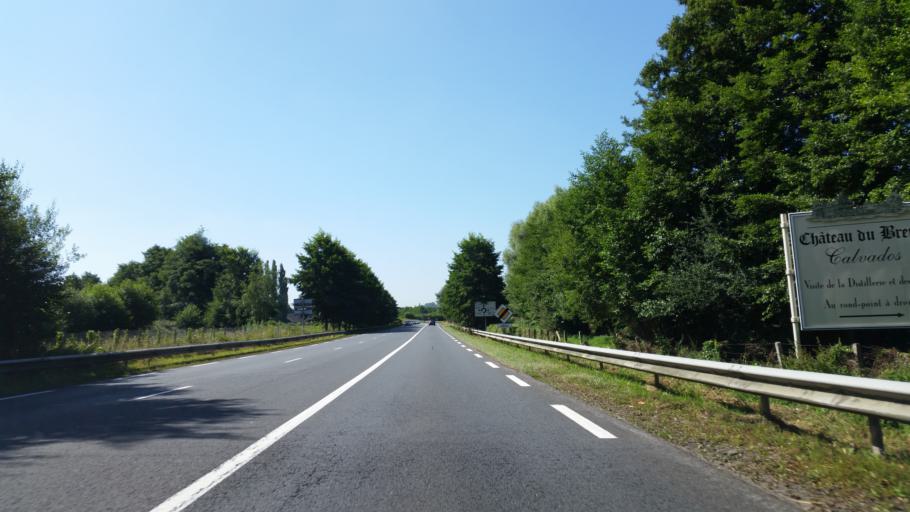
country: FR
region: Lower Normandy
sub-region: Departement du Calvados
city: Lisieux
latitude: 49.2332
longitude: 0.2195
